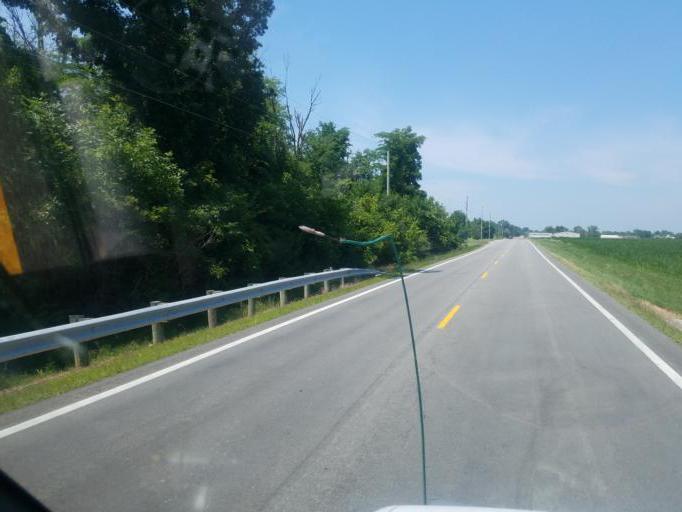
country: US
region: Ohio
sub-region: Auglaize County
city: Saint Marys
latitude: 40.4997
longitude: -84.4346
